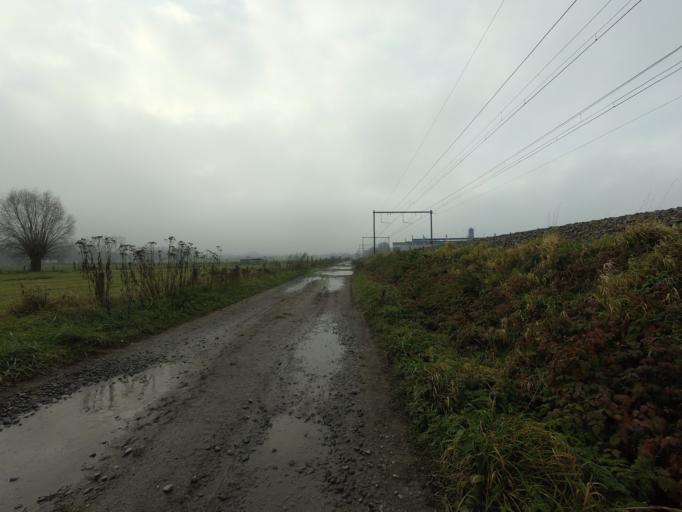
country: BE
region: Flanders
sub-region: Provincie Oost-Vlaanderen
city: Geraardsbergen
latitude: 50.7931
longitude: 3.8887
